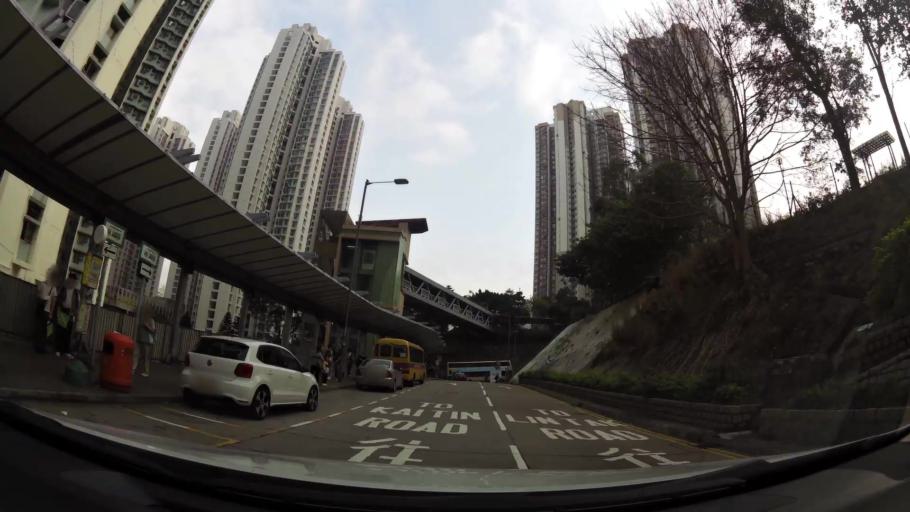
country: HK
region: Kowloon City
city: Kowloon
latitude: 22.3092
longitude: 114.2355
